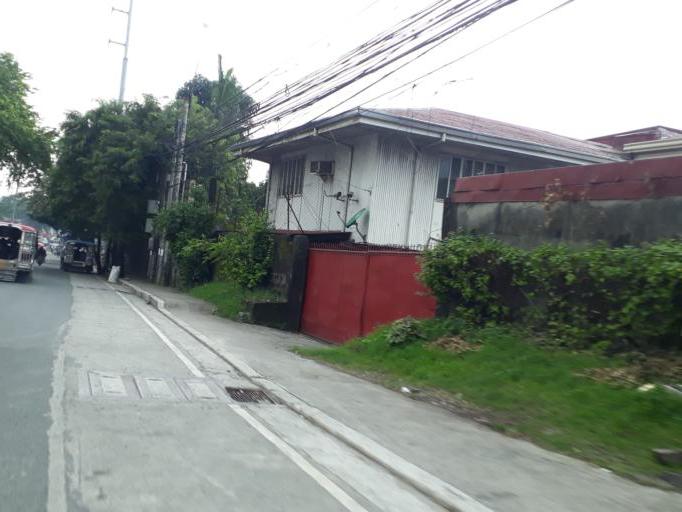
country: PH
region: Calabarzon
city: Bagong Pagasa
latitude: 14.6712
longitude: 121.0516
